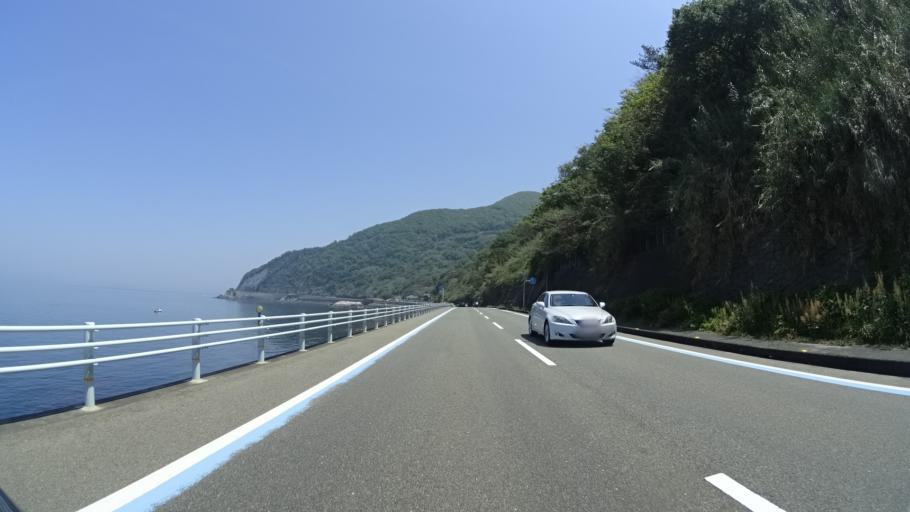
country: JP
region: Ehime
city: Ozu
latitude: 33.5861
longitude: 132.4527
